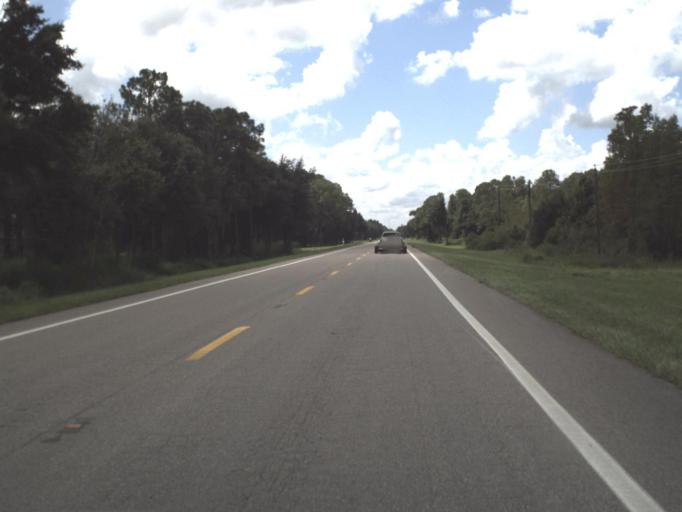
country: US
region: Florida
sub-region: Polk County
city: Polk City
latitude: 28.2324
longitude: -81.8208
